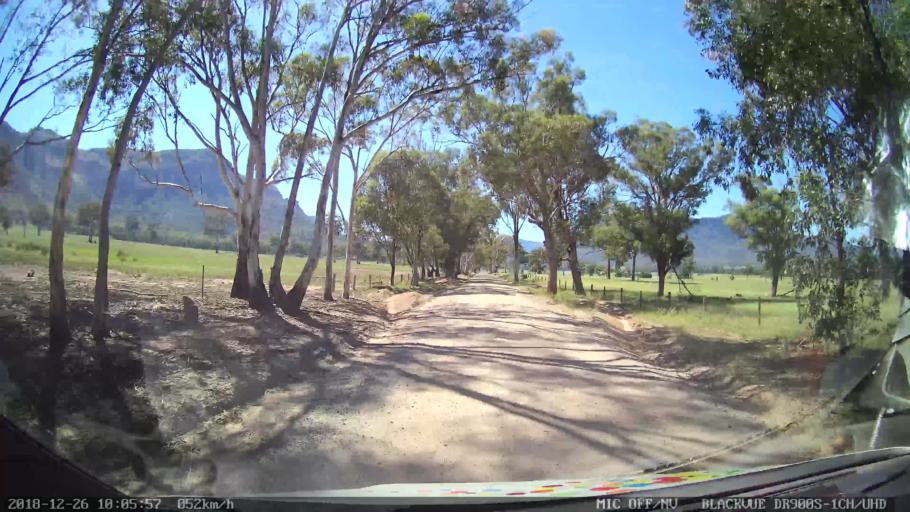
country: AU
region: New South Wales
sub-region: Mid-Western Regional
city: Kandos
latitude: -33.0815
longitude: 150.2151
